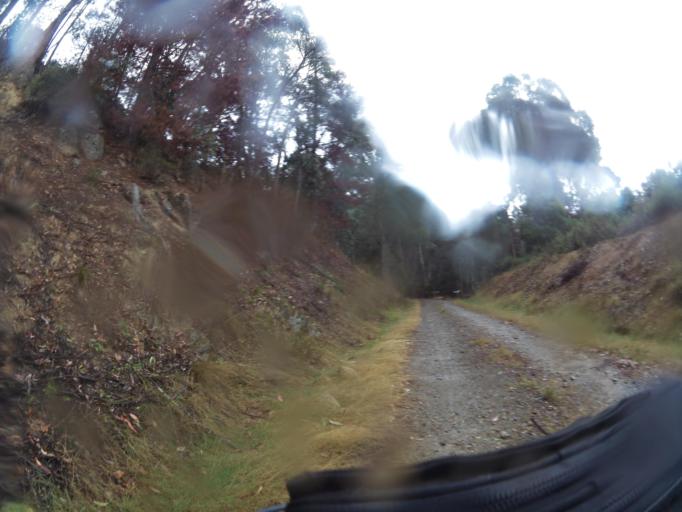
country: AU
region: New South Wales
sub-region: Greater Hume Shire
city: Holbrook
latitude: -36.2165
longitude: 147.5660
